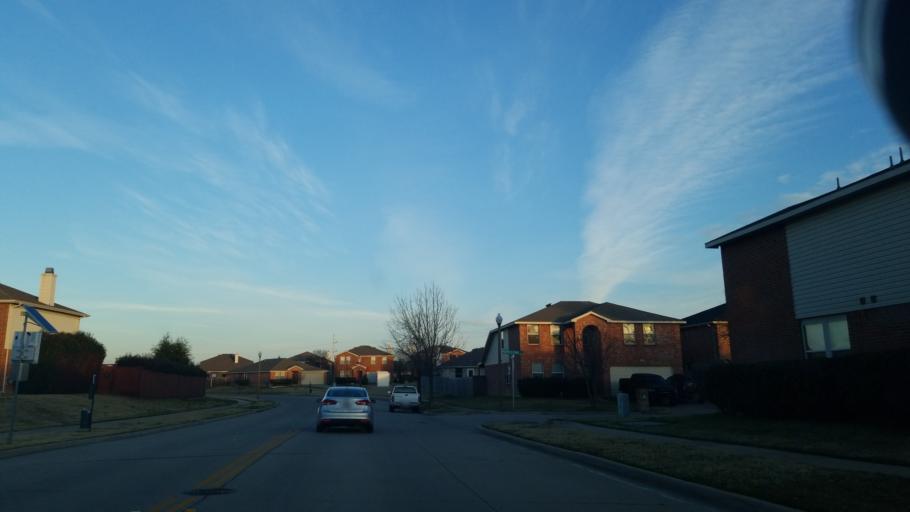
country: US
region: Texas
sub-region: Denton County
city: Corinth
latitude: 33.1538
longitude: -97.0998
